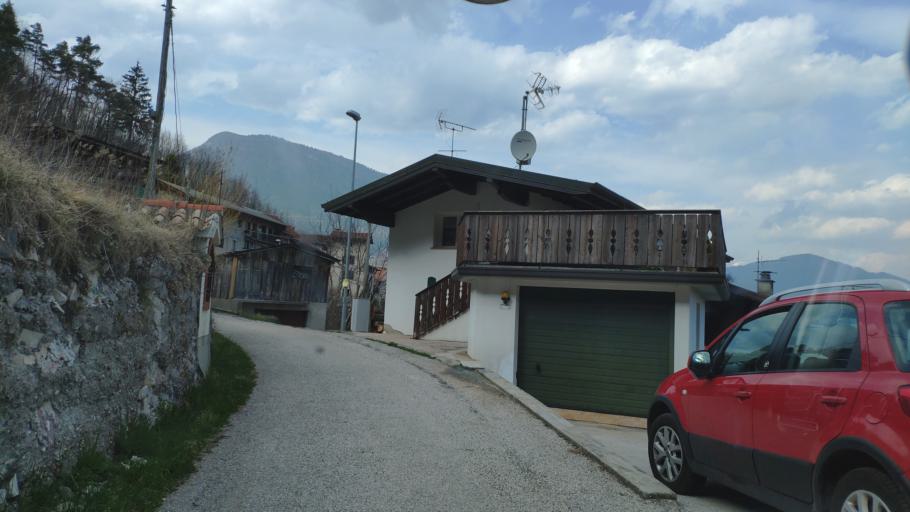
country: IT
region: Veneto
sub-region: Provincia di Vicenza
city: Enego
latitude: 45.9543
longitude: 11.7036
